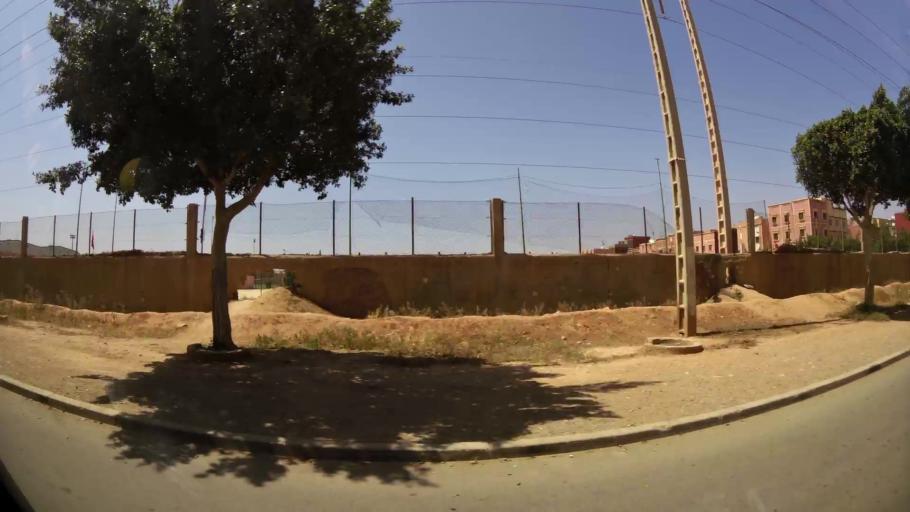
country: MA
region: Souss-Massa-Draa
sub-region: Inezgane-Ait Mellou
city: Inezgane
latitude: 30.3456
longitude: -9.4889
